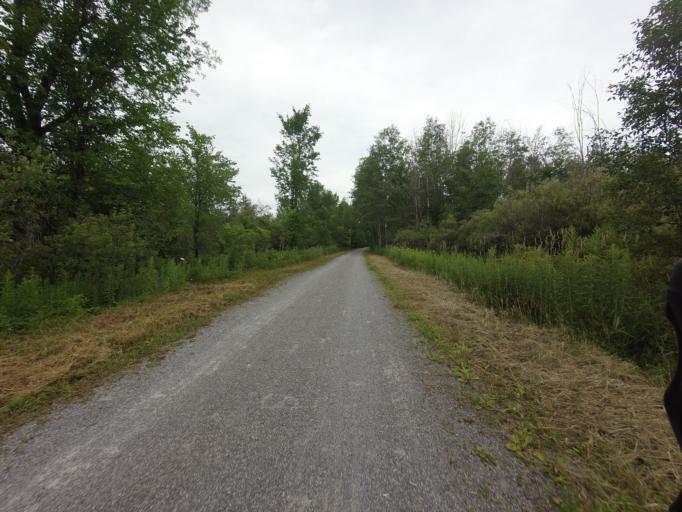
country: CA
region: Ontario
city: Ottawa
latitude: 45.2114
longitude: -75.6249
